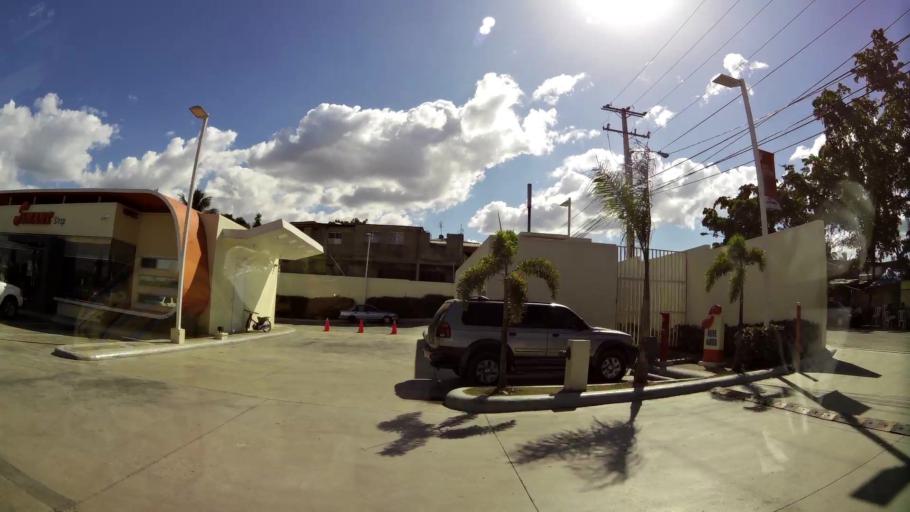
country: DO
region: Santo Domingo
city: Santo Domingo Oeste
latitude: 18.5453
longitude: -70.0392
